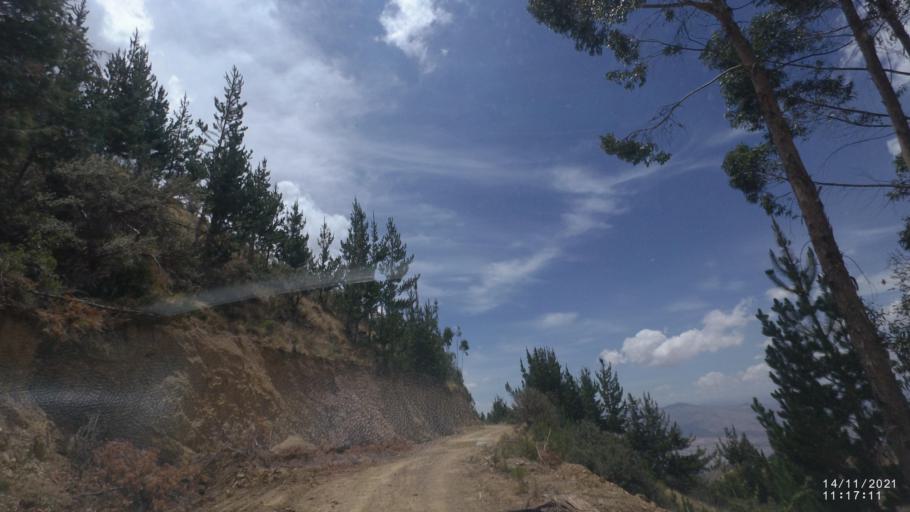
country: BO
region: Cochabamba
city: Cochabamba
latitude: -17.3301
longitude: -66.0458
